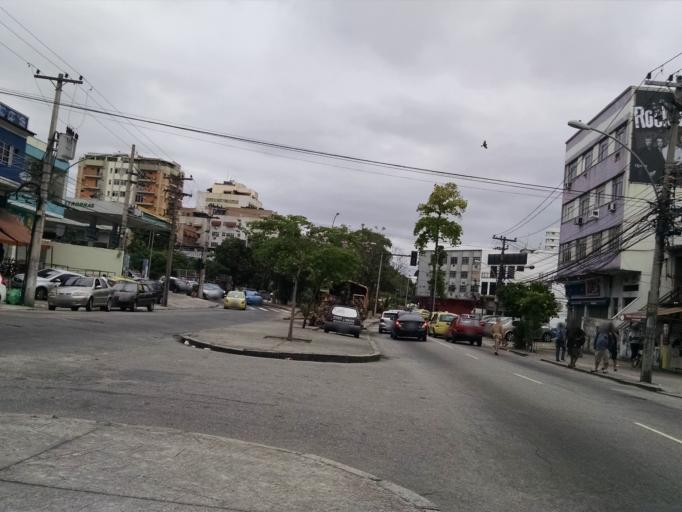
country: BR
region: Rio de Janeiro
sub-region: Duque De Caxias
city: Duque de Caxias
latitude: -22.8384
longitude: -43.3107
